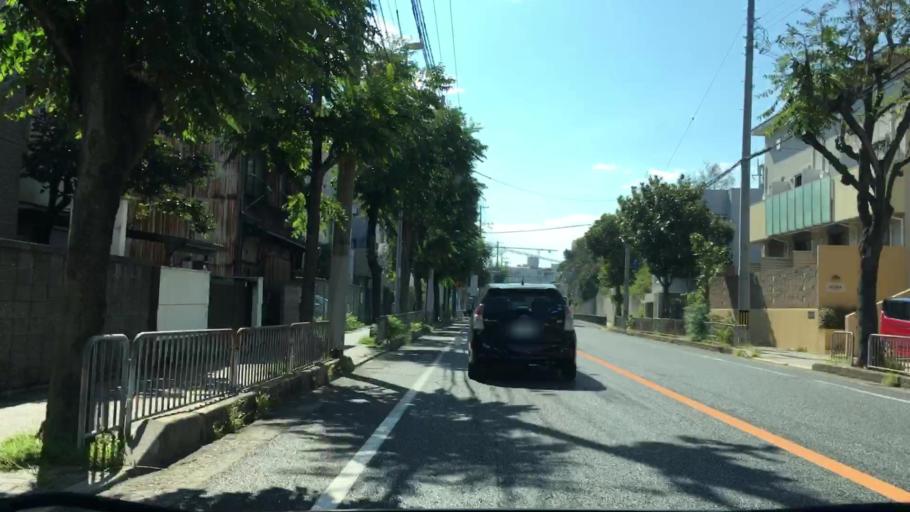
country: JP
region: Hyogo
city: Akashi
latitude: 34.6283
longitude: 135.0470
